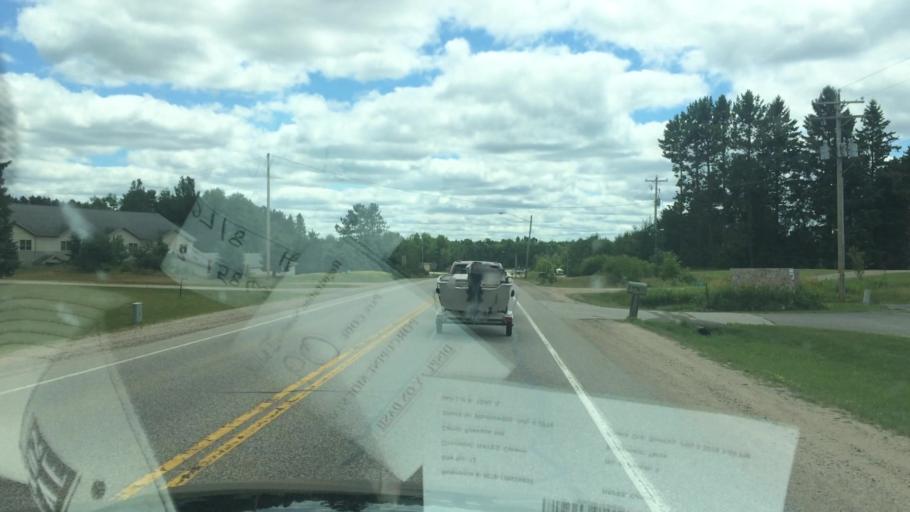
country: US
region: Wisconsin
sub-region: Vilas County
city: Eagle River
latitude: 45.7895
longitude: -89.3205
